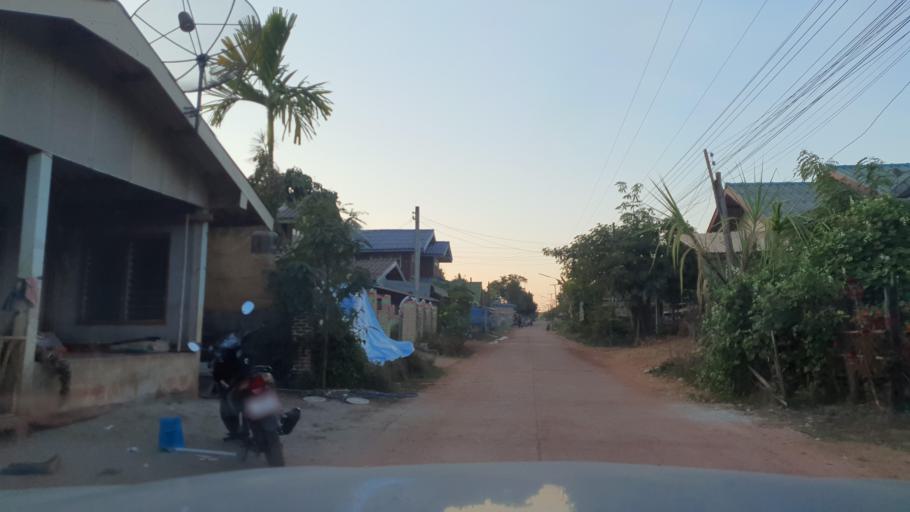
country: TH
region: Nakhon Phanom
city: Ban Phaeng
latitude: 17.8280
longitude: 104.2670
